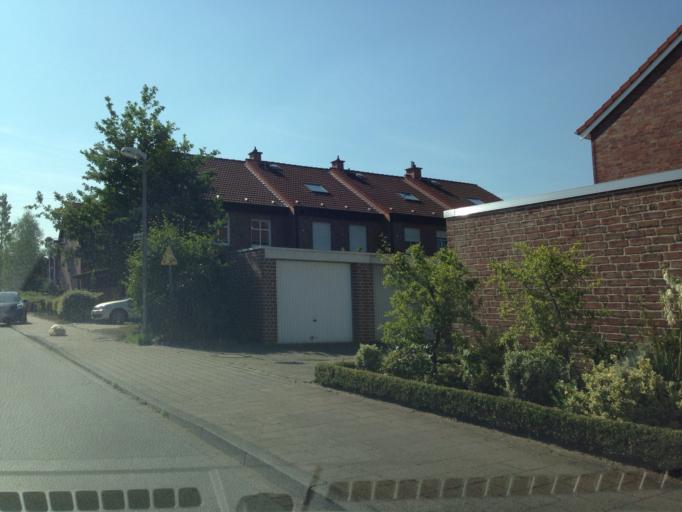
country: DE
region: North Rhine-Westphalia
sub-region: Regierungsbezirk Munster
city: Muenster
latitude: 51.9926
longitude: 7.6023
